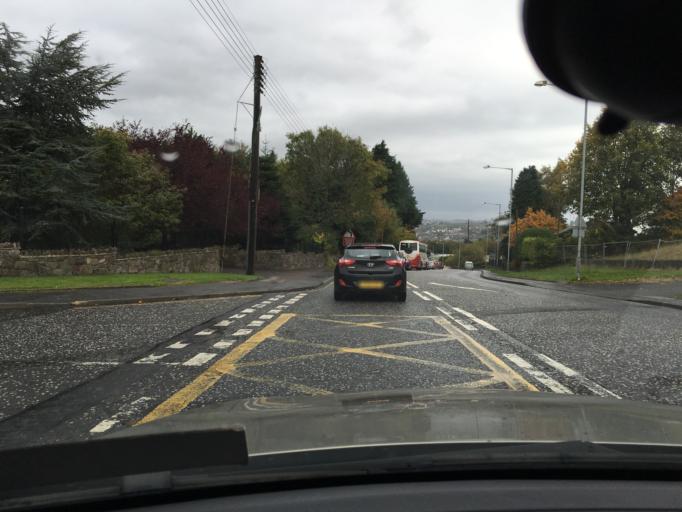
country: GB
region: Northern Ireland
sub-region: Newry and Mourne District
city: Newry
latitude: 54.1637
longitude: -6.3451
